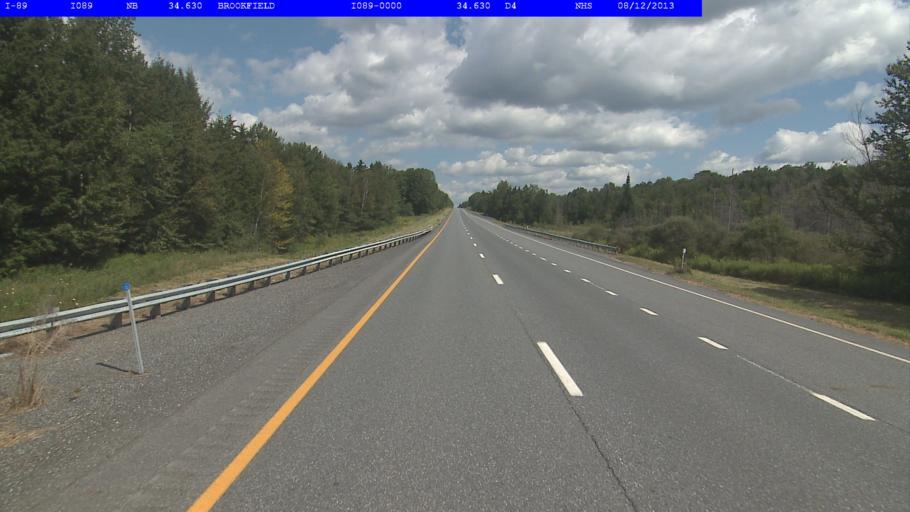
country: US
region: Vermont
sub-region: Orange County
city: Randolph
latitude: 43.9980
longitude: -72.6229
